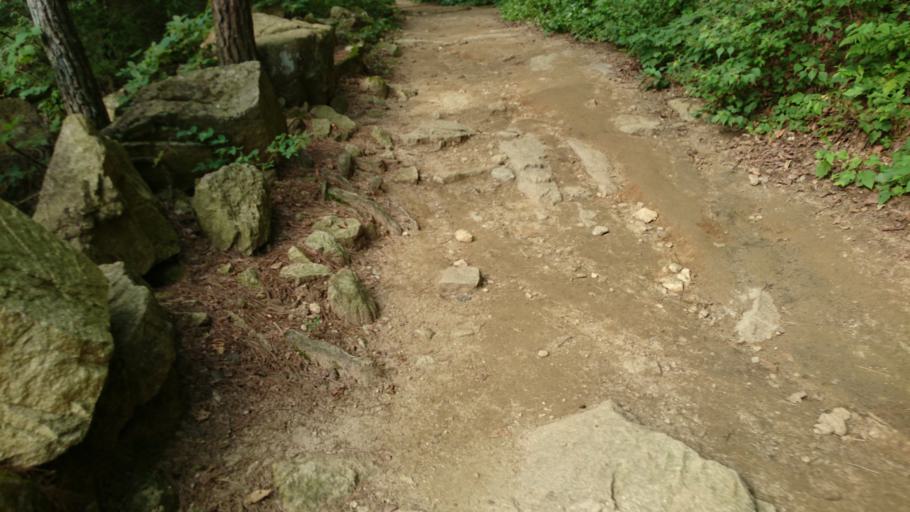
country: KR
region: Daegu
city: Daegu
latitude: 35.9960
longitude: 128.6826
